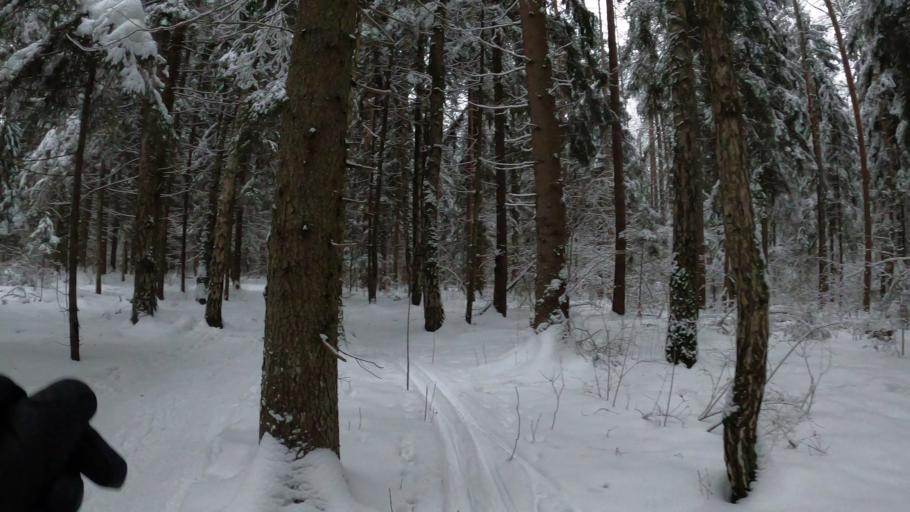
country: RU
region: Moskovskaya
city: Firsanovka
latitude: 55.9309
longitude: 37.2202
